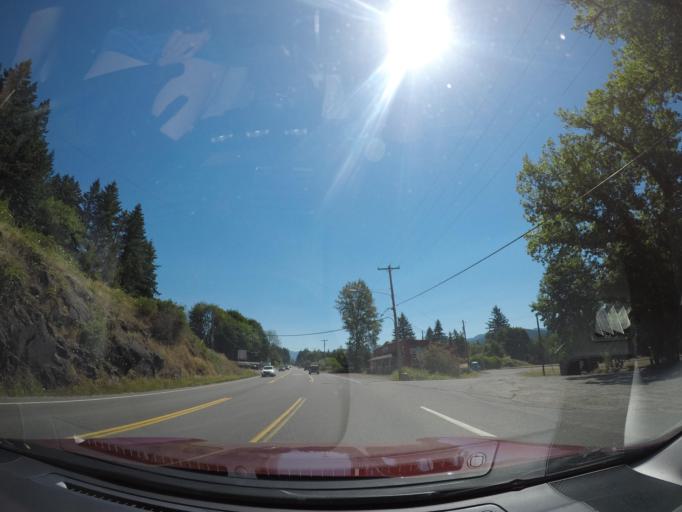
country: US
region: Oregon
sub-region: Linn County
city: Mill City
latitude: 44.7557
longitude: -122.4753
